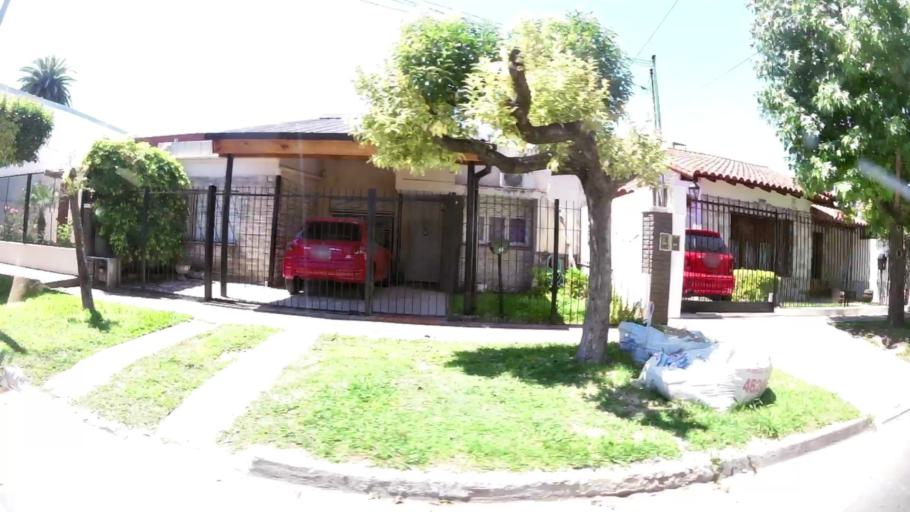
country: AR
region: Buenos Aires
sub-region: Partido de Merlo
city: Merlo
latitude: -34.6627
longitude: -58.6928
